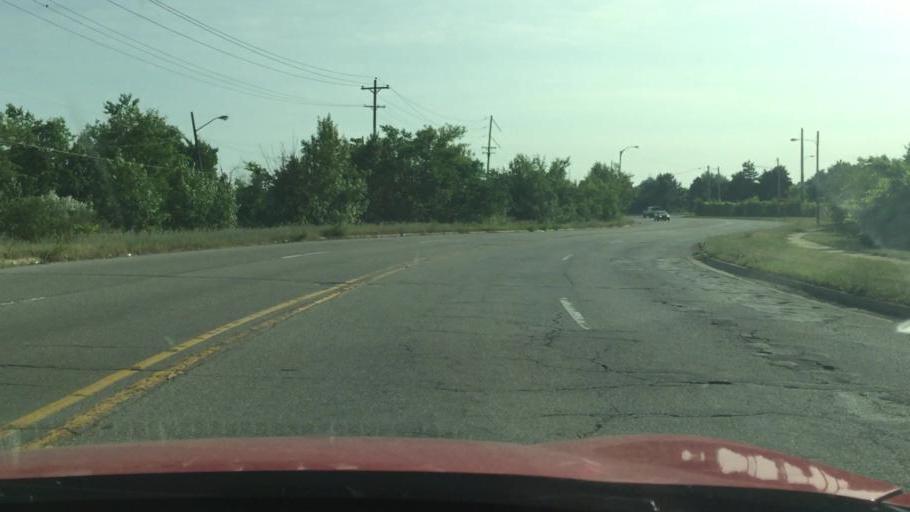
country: US
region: Michigan
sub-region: Genesee County
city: Flint
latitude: 43.0359
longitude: -83.6814
